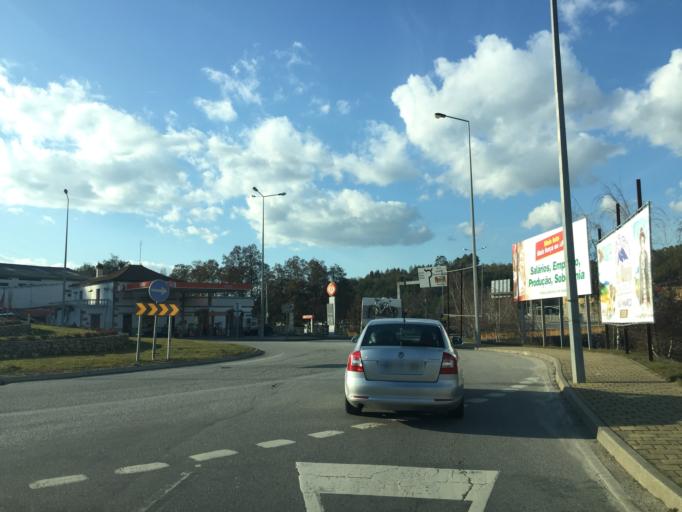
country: PT
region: Guarda
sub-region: Seia
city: Seia
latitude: 40.4311
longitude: -7.7178
